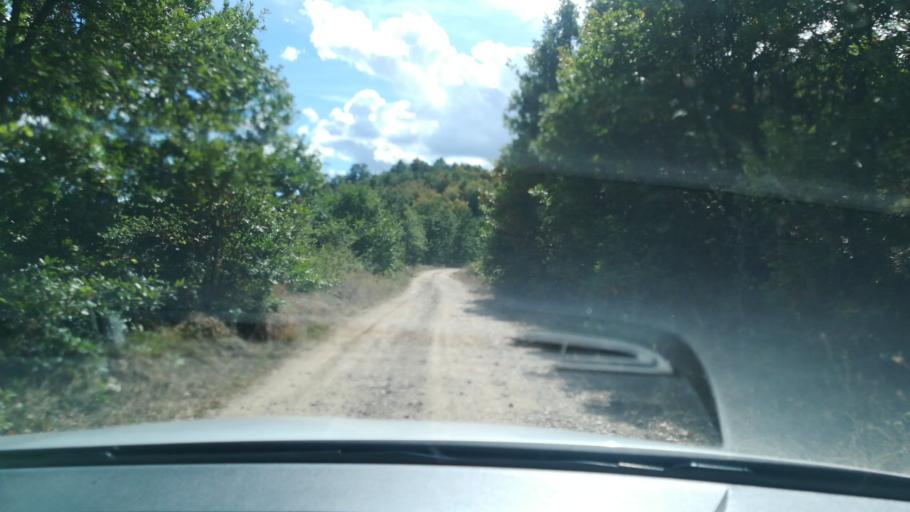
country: MK
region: Delcevo
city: Delcevo
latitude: 41.8981
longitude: 22.8053
